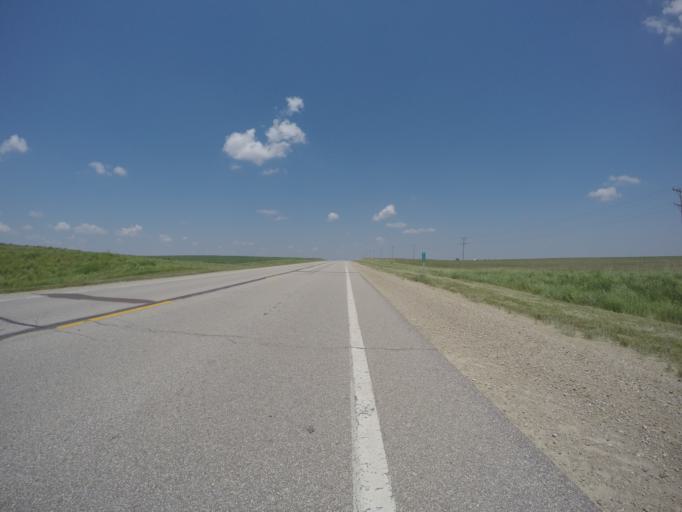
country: US
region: Kansas
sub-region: Doniphan County
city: Troy
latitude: 39.7479
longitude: -95.1438
